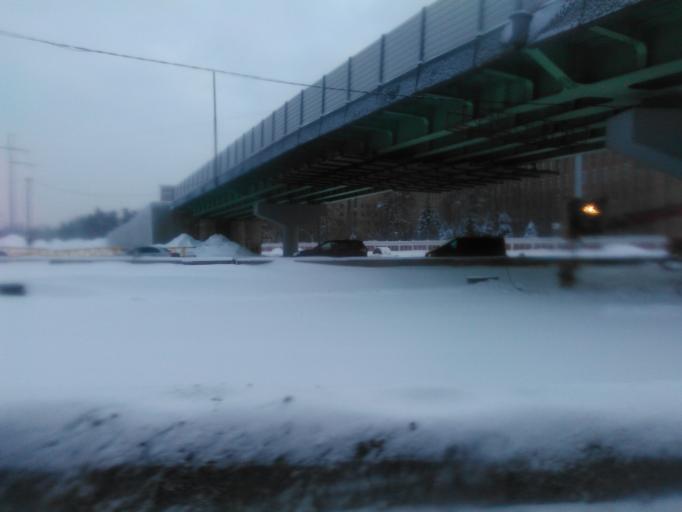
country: RU
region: Moskovskaya
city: Bolshevo
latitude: 55.9313
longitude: 37.8042
